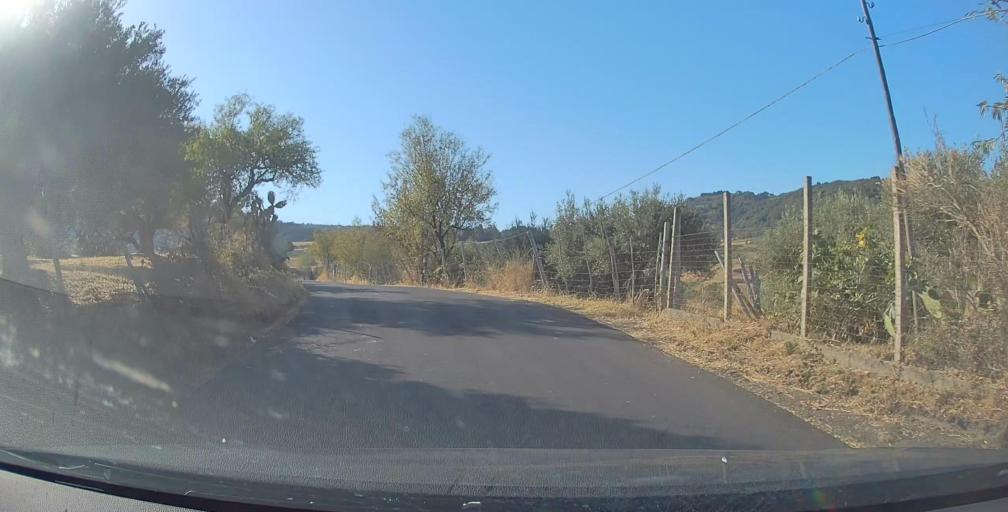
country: IT
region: Sicily
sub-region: Messina
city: San Piero Patti
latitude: 38.0617
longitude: 14.9898
